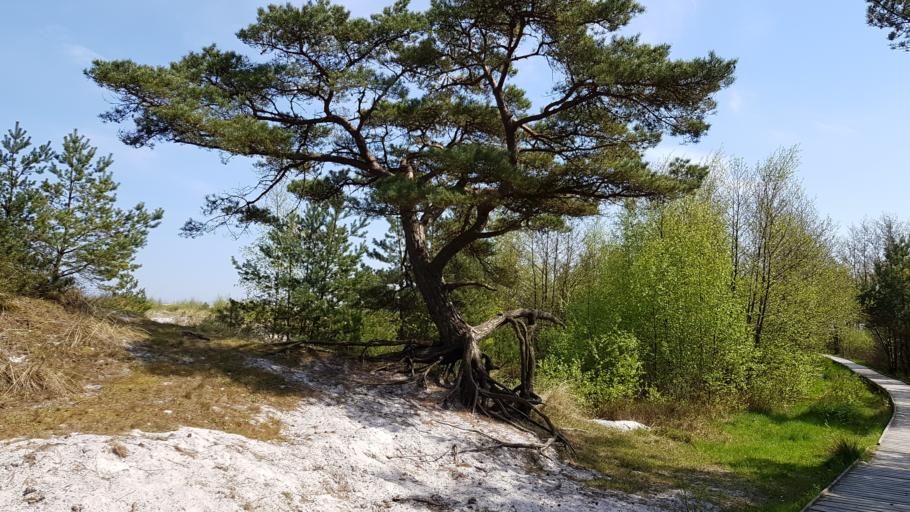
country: DK
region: Capital Region
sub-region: Bornholm Kommune
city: Nexo
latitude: 54.9954
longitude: 15.0871
